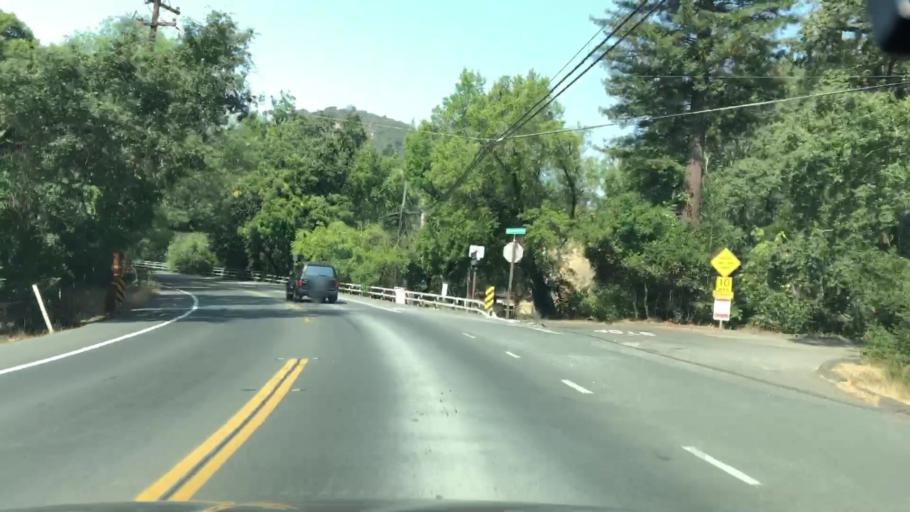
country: US
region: California
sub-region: Sonoma County
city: Larkfield-Wikiup
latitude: 38.5498
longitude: -122.7191
